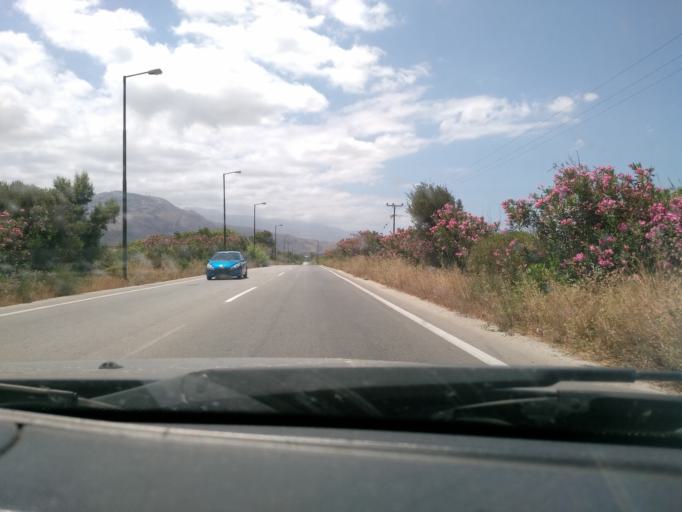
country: GR
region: Crete
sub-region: Nomos Chanias
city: Georgioupolis
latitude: 35.3507
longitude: 24.3071
